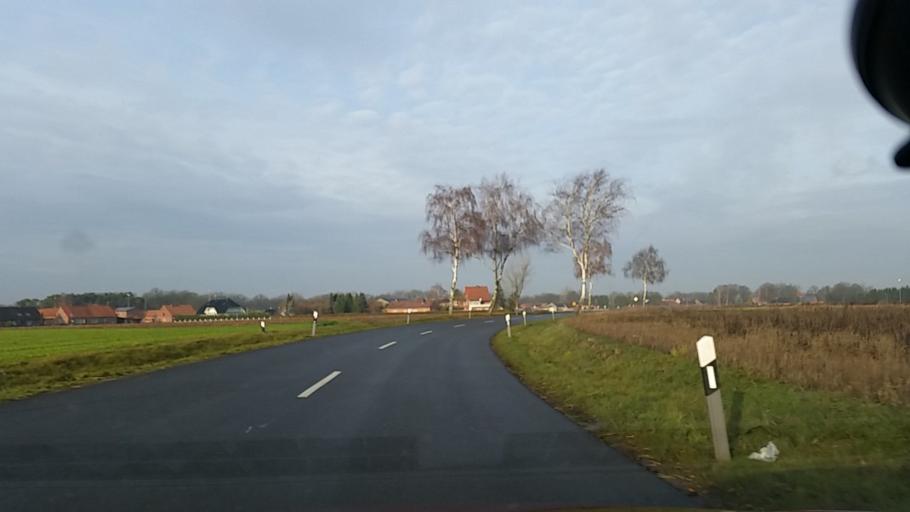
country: DE
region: Lower Saxony
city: Luder
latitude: 52.8037
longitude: 10.6723
